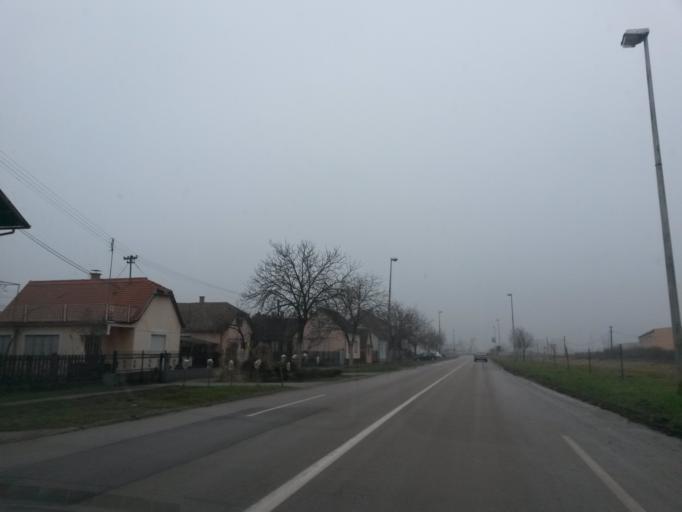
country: HR
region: Vukovarsko-Srijemska
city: Zupanja
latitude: 45.0935
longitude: 18.6974
